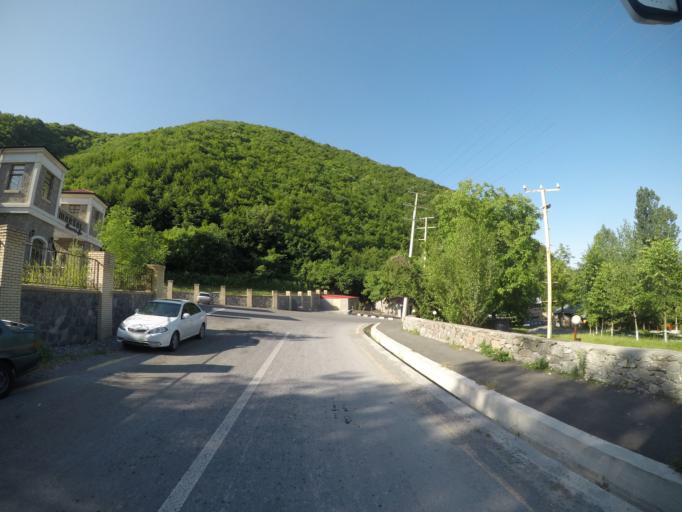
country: AZ
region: Shaki City
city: Sheki
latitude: 41.2445
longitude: 47.2002
